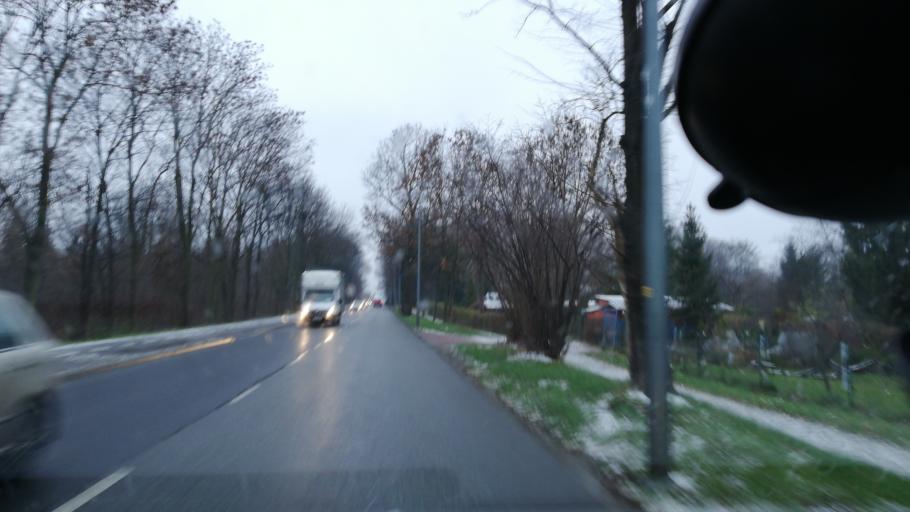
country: PL
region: Silesian Voivodeship
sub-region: Chorzow
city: Chorzow
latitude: 50.2999
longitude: 18.9859
